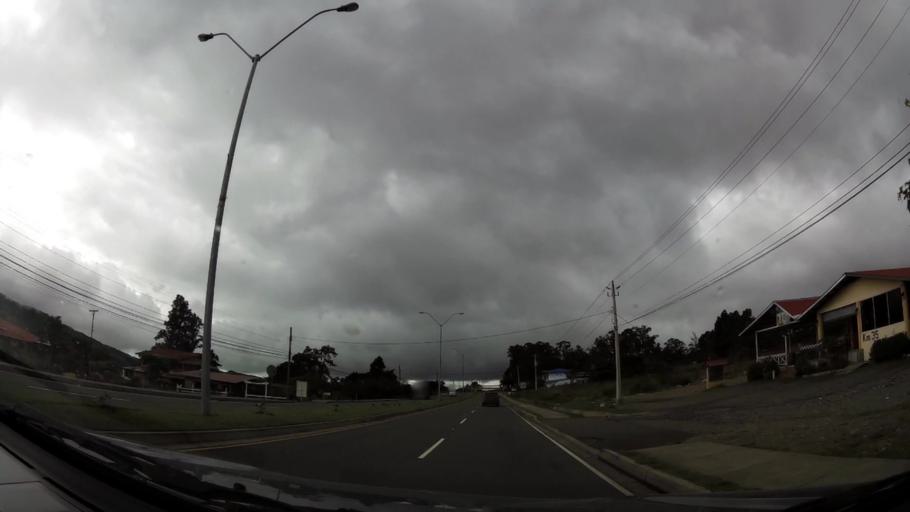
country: PA
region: Chiriqui
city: Palmira
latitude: 8.7490
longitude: -82.4323
